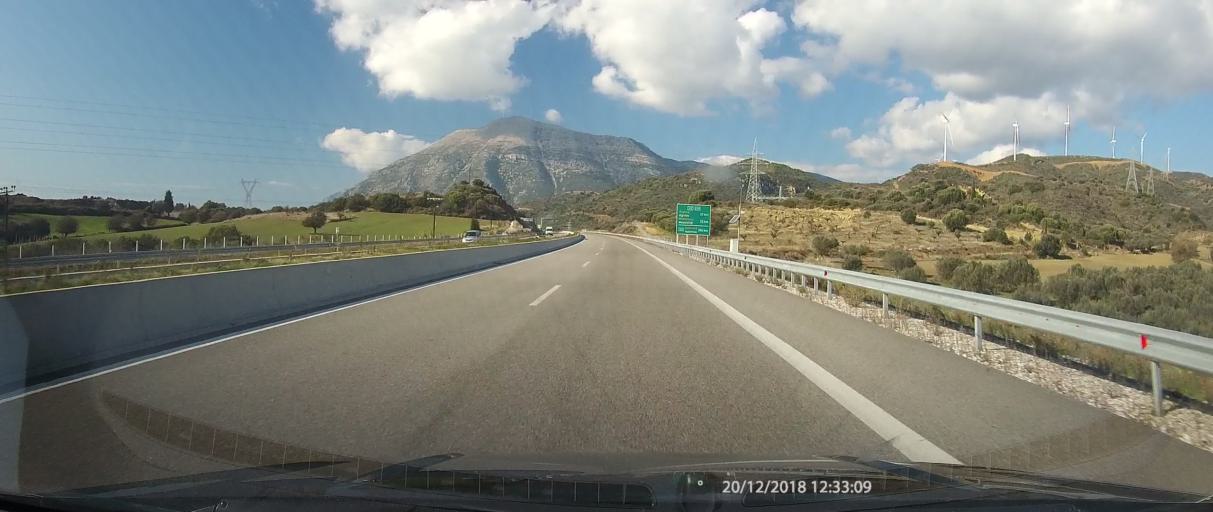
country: GR
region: West Greece
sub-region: Nomos Aitolias kai Akarnanias
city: Antirrio
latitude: 38.3482
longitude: 21.7491
